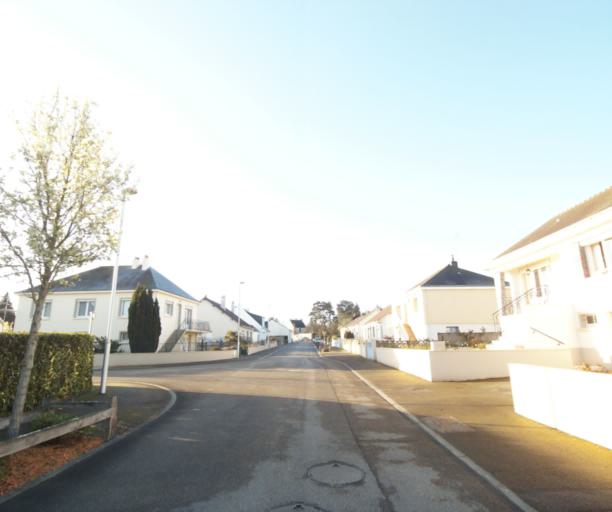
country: FR
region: Pays de la Loire
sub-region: Departement de la Loire-Atlantique
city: Bouvron
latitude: 47.4169
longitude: -1.8490
